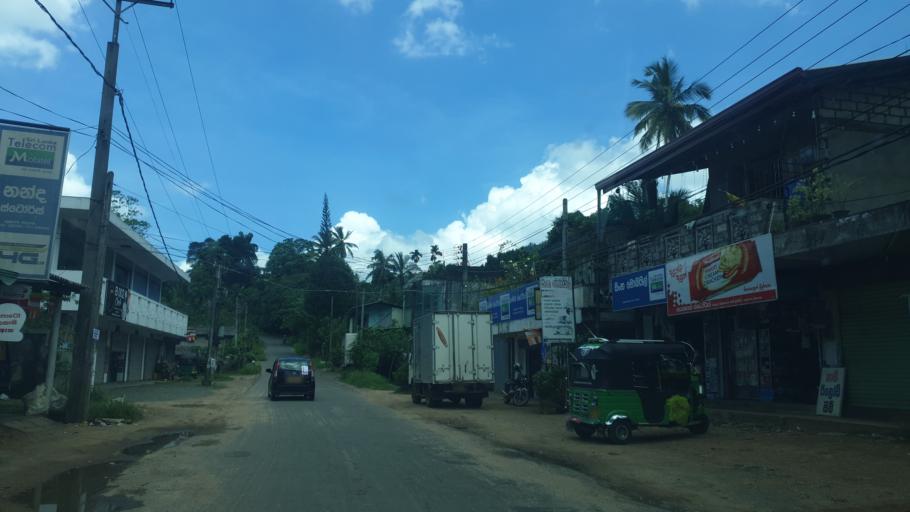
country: LK
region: Sabaragamuwa
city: Ratnapura
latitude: 6.4916
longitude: 80.3984
